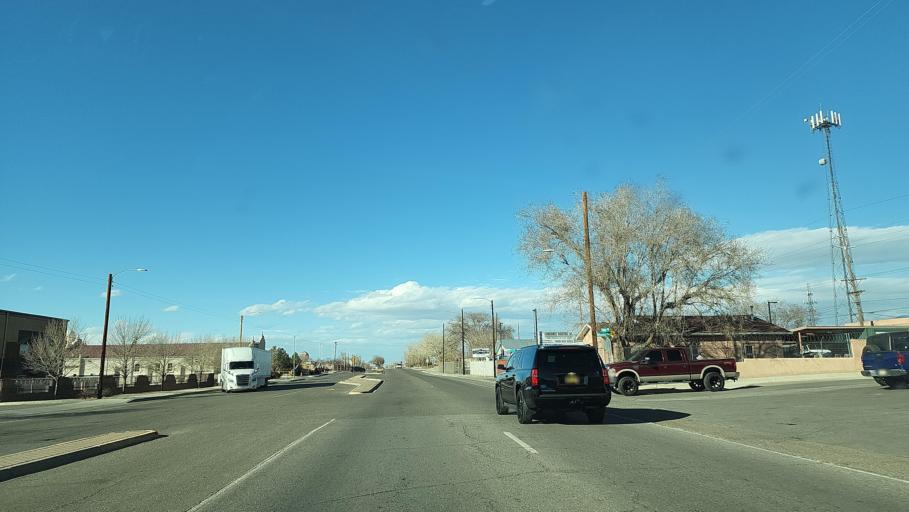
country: US
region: New Mexico
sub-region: Bernalillo County
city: Albuquerque
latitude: 35.0563
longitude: -106.6451
